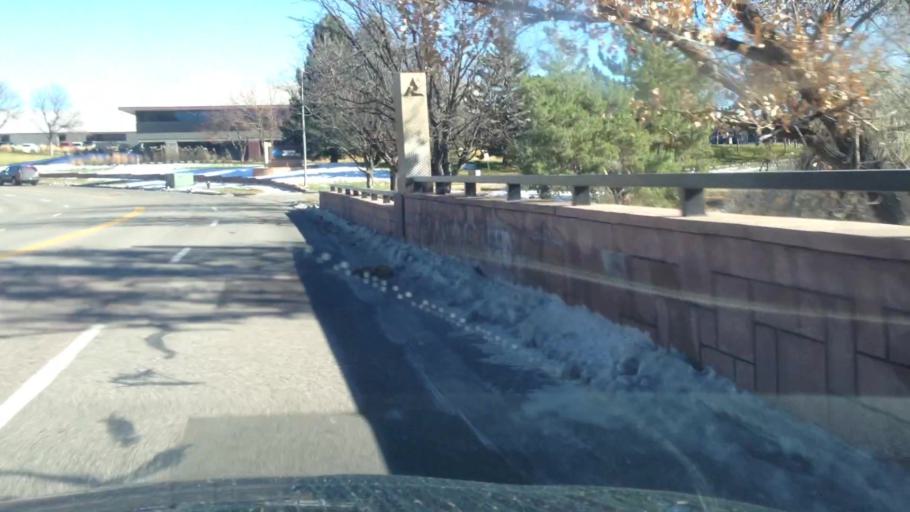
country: US
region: Colorado
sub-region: Douglas County
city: Meridian
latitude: 39.5715
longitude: -104.8578
